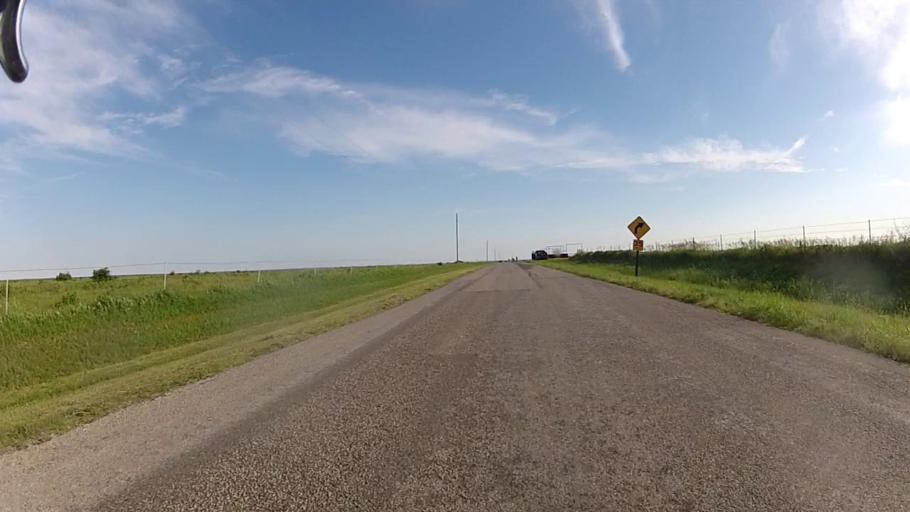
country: US
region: Kansas
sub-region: Cowley County
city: Arkansas City
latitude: 37.0524
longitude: -96.8230
